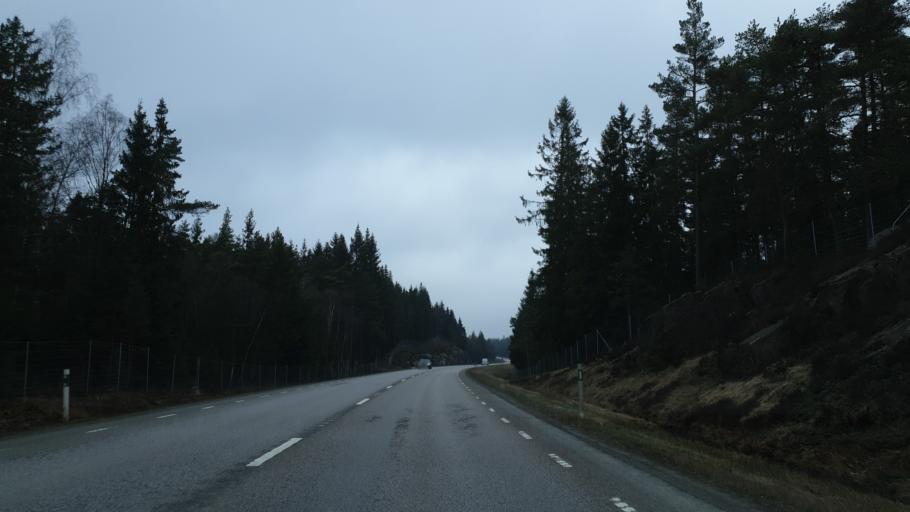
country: SE
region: Vaestra Goetaland
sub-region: Harryda Kommun
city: Hindas
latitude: 57.6589
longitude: 12.3718
